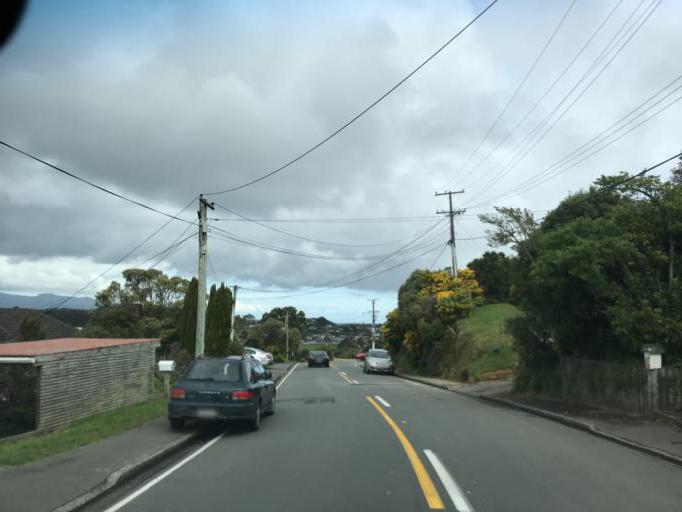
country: NZ
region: Wellington
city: Petone
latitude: -41.2179
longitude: 174.7996
